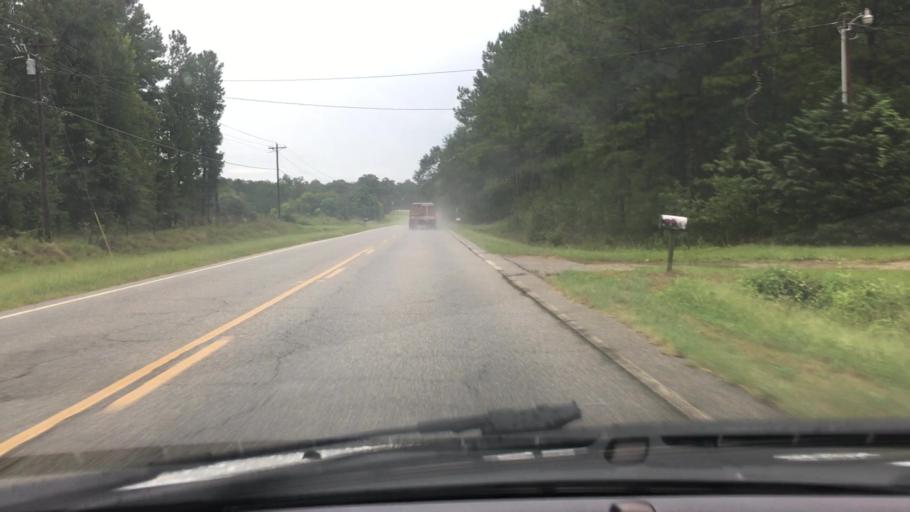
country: US
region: Georgia
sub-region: Grady County
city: Cairo
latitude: 30.7882
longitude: -84.2701
